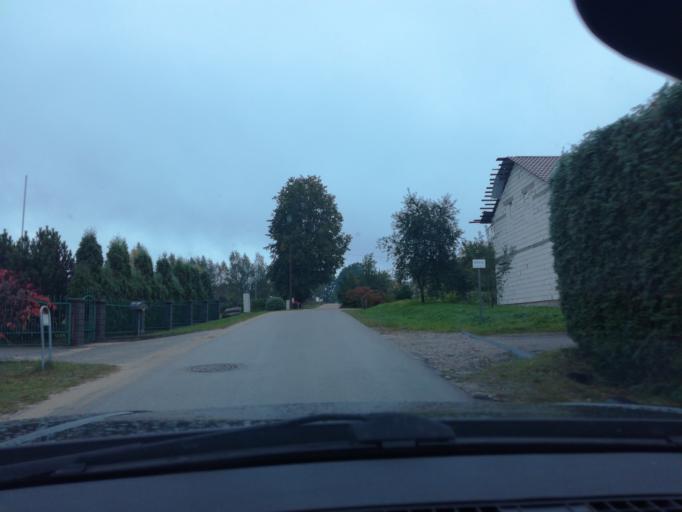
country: LT
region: Alytaus apskritis
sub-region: Alytus
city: Alytus
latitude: 54.3946
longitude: 24.0978
